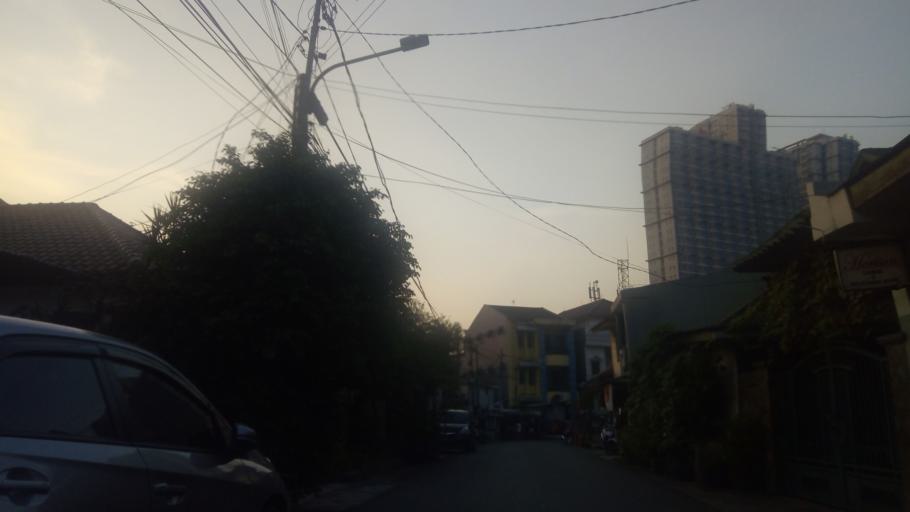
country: ID
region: Jakarta Raya
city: Jakarta
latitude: -6.2009
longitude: 106.8494
